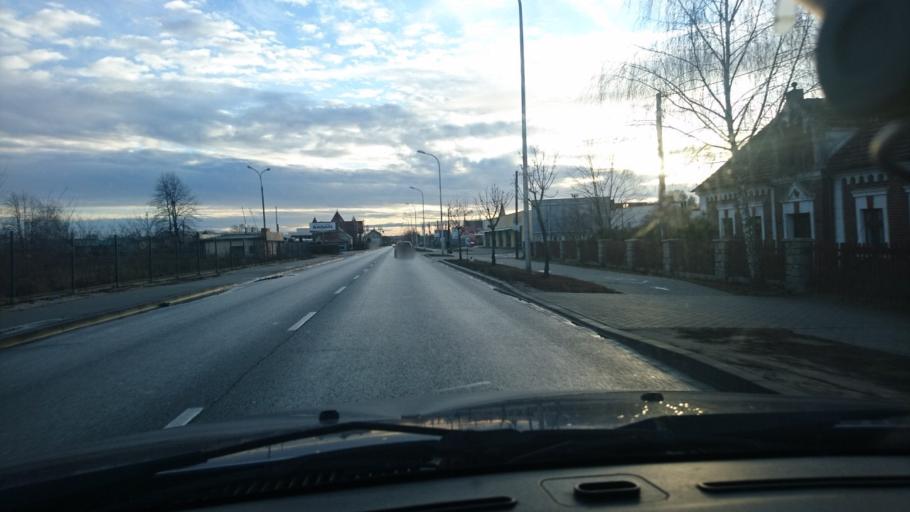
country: PL
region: Greater Poland Voivodeship
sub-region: Powiat kepinski
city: Kepno
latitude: 51.2947
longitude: 17.9962
